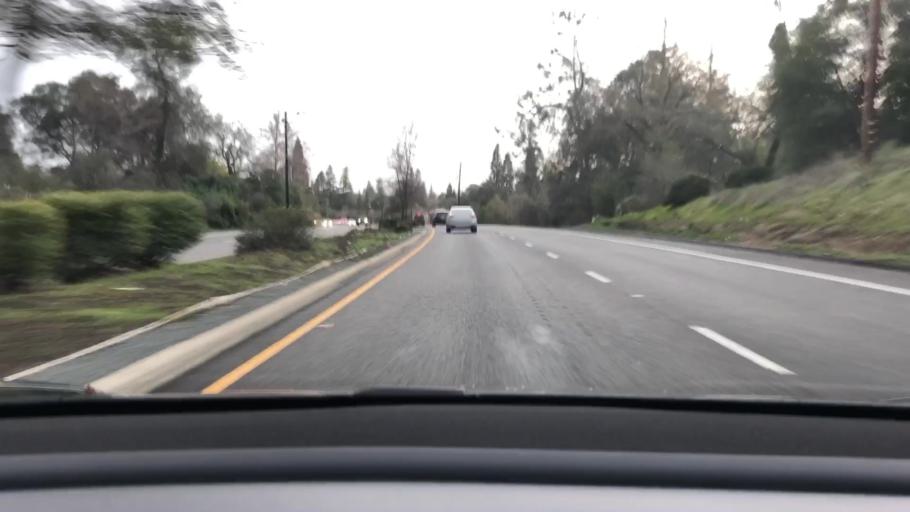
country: US
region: California
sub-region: Sacramento County
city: Folsom
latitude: 38.7165
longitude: -121.1759
